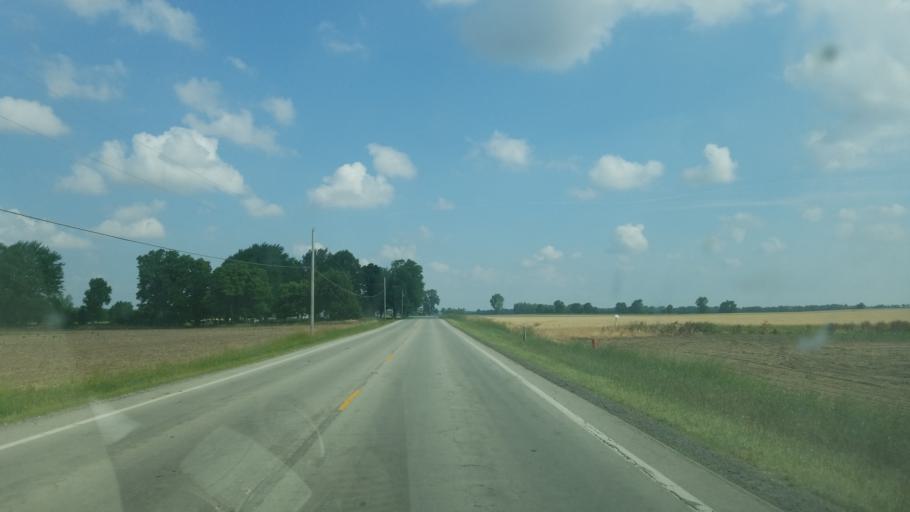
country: US
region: Ohio
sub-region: Logan County
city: Russells Point
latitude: 40.5239
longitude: -83.8283
